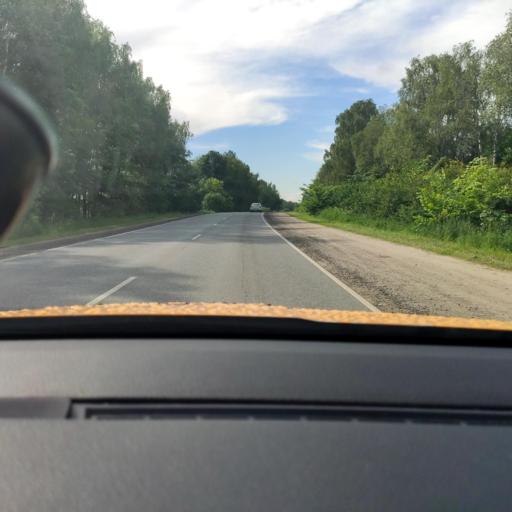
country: RU
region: Moskovskaya
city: Zhilevo
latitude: 54.9482
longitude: 38.0111
